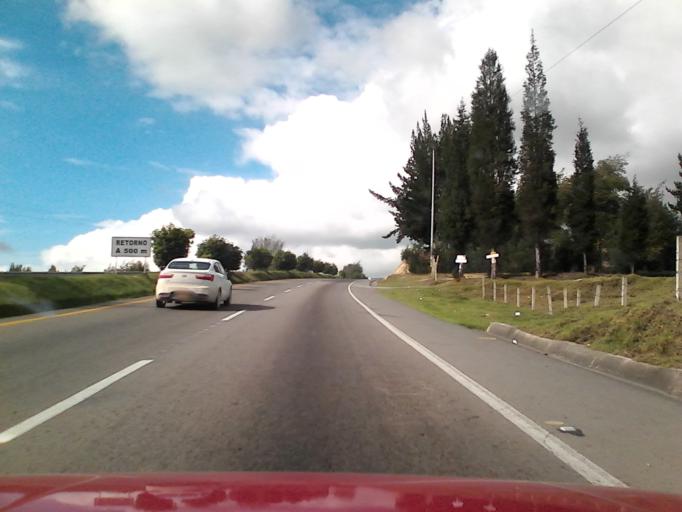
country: CO
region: Boyaca
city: Combita
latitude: 5.6304
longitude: -73.2994
